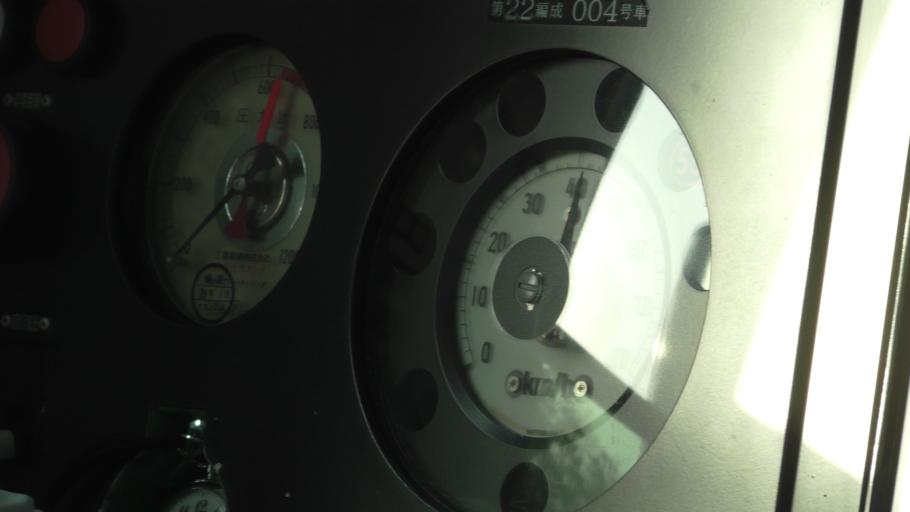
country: JP
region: Chiba
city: Chiba
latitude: 35.6400
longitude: 140.1122
